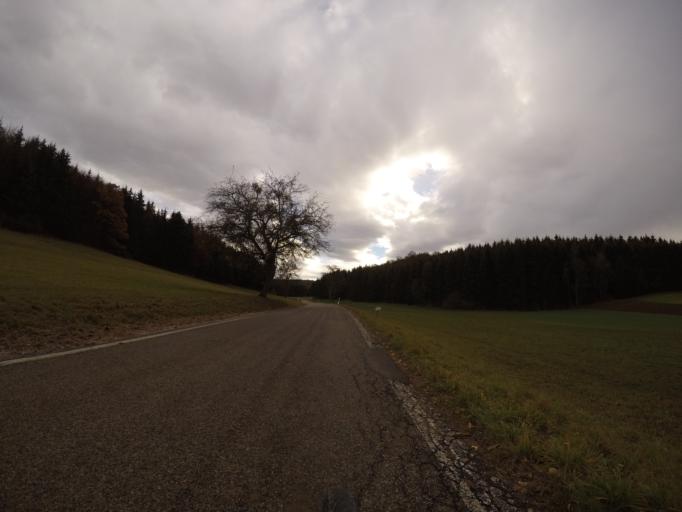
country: DE
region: Baden-Wuerttemberg
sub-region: Tuebingen Region
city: Sankt Johann
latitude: 48.4143
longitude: 9.2921
